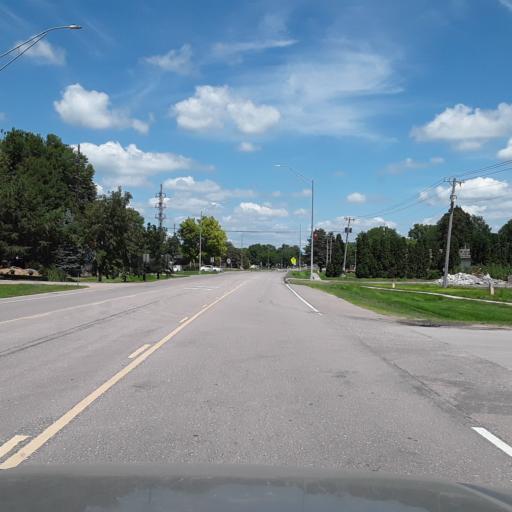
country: US
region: Nebraska
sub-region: Merrick County
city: Central City
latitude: 41.1033
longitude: -98.0016
